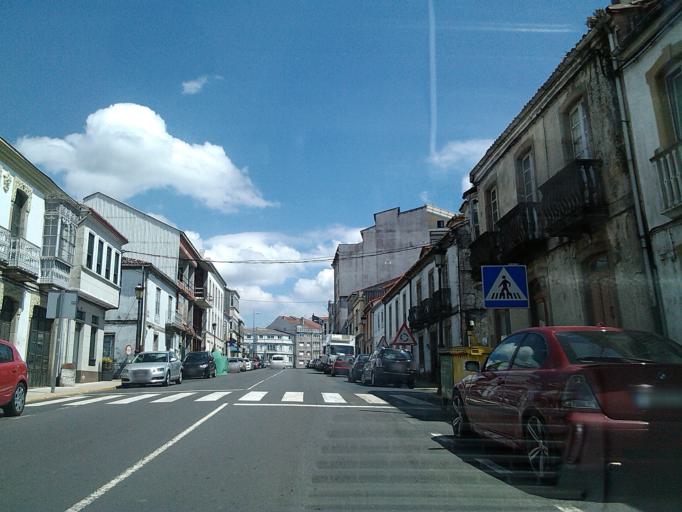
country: ES
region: Galicia
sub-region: Provincia da Coruna
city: Melide
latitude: 42.9133
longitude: -8.0168
